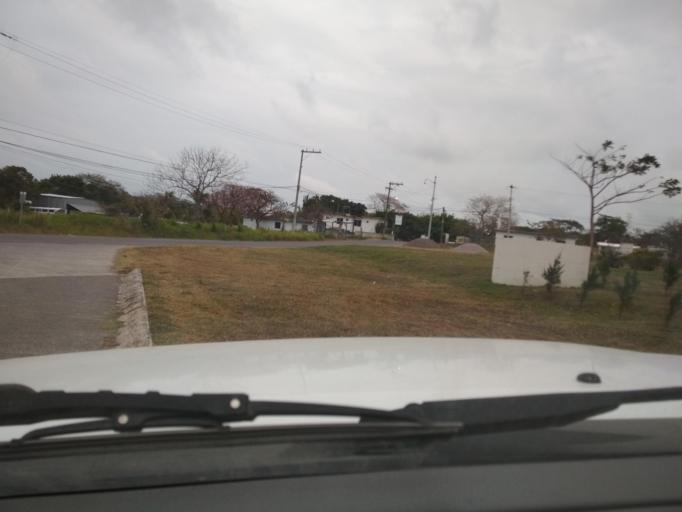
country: MX
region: Veracruz
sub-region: Medellin
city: Fraccionamiento Arboledas San Ramon
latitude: 19.0900
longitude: -96.1304
